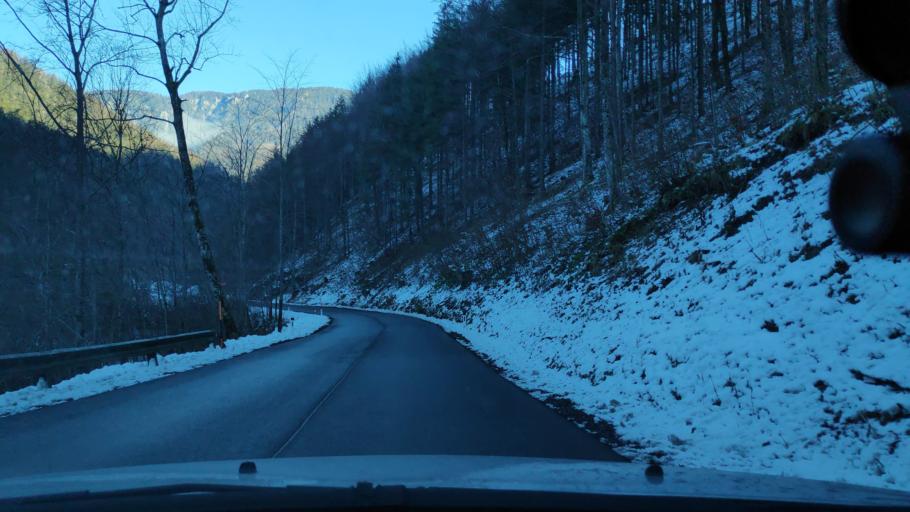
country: AT
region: Lower Austria
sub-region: Politischer Bezirk Neunkirchen
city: Schwarzau im Gebirge
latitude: 47.7688
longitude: 15.7162
